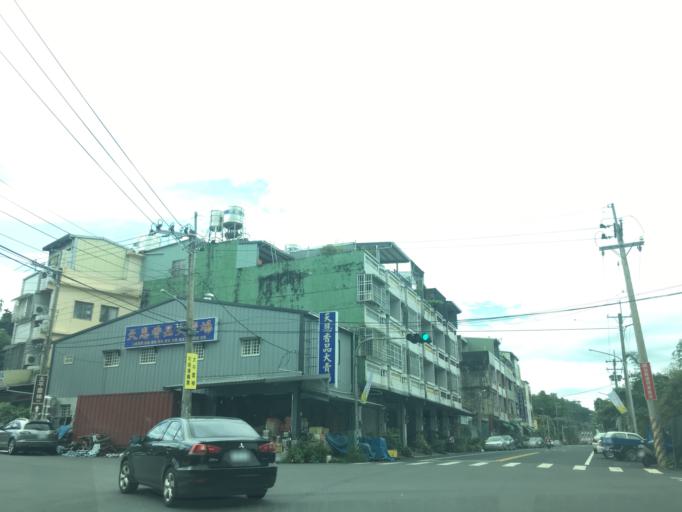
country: TW
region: Taiwan
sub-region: Yunlin
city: Douliu
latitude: 23.5823
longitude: 120.5613
